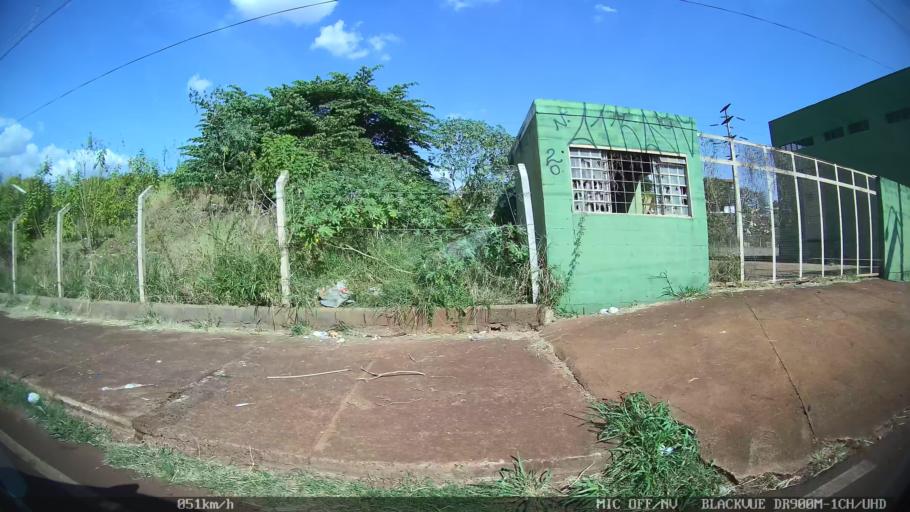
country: BR
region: Sao Paulo
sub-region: Ribeirao Preto
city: Ribeirao Preto
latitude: -21.1784
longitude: -47.8312
